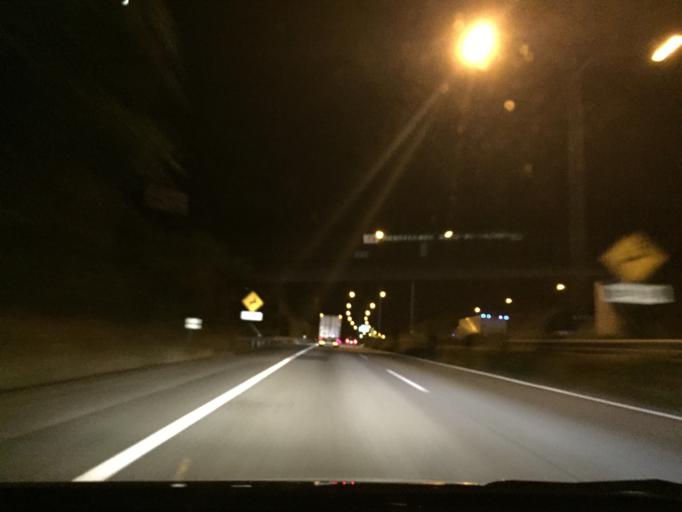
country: JP
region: Kanagawa
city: Hadano
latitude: 35.3541
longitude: 139.1196
